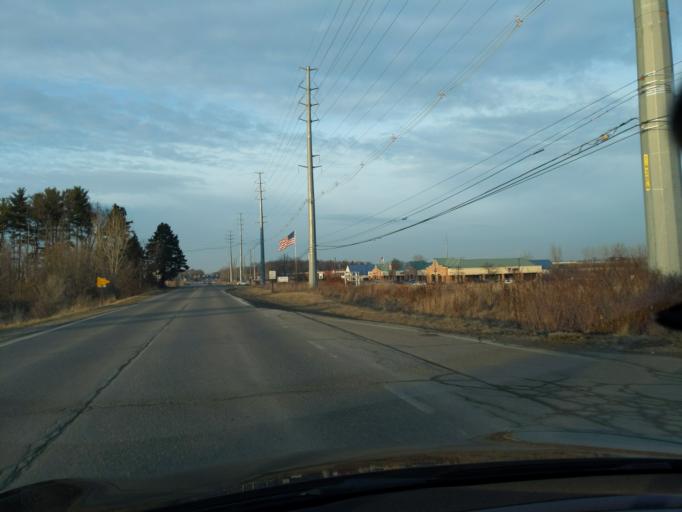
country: US
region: Michigan
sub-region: Livingston County
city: Brighton
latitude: 42.6287
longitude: -83.7527
